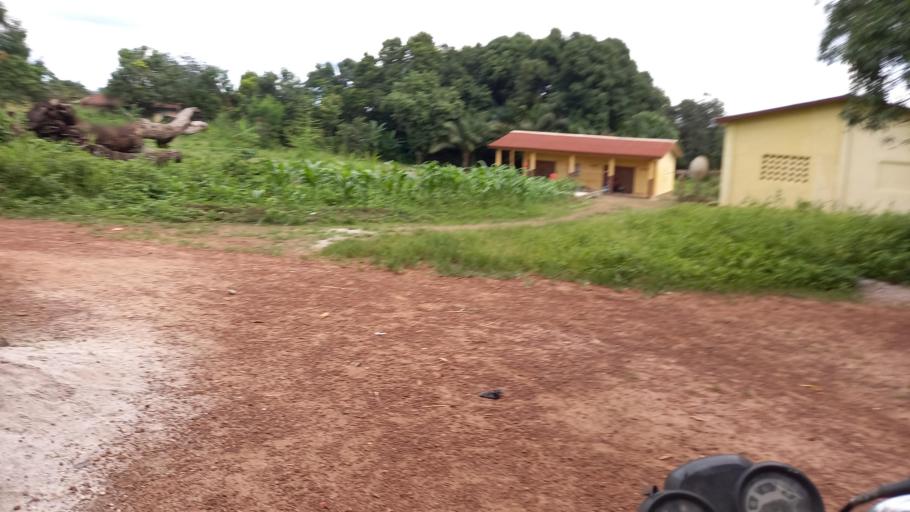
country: SL
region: Northern Province
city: Kamakwie
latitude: 9.5111
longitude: -12.2415
